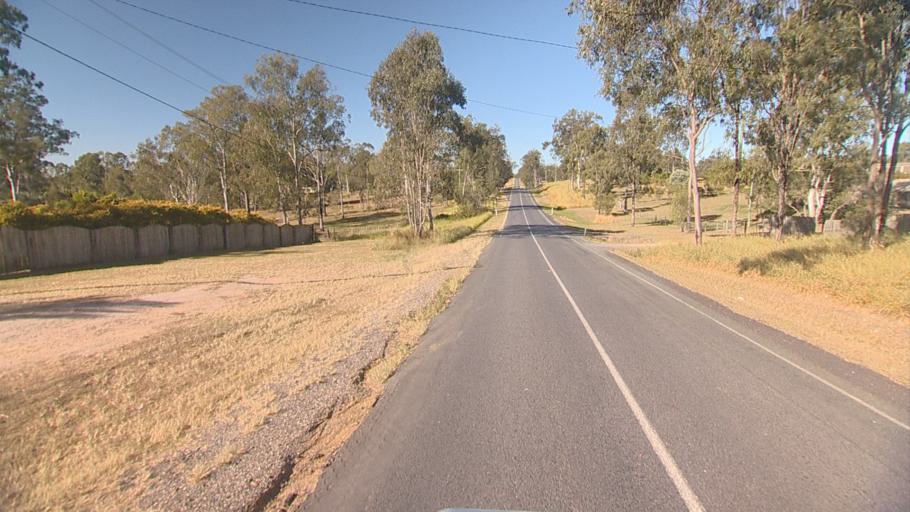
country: AU
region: Queensland
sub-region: Logan
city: North Maclean
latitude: -27.7913
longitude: 153.0172
